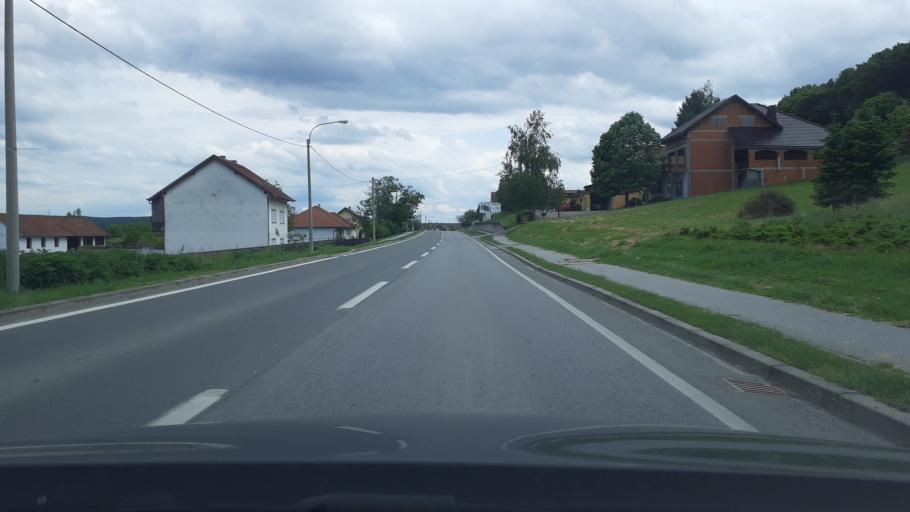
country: HR
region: Pozesko-Slavonska
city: Pleternica
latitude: 45.3012
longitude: 17.7920
